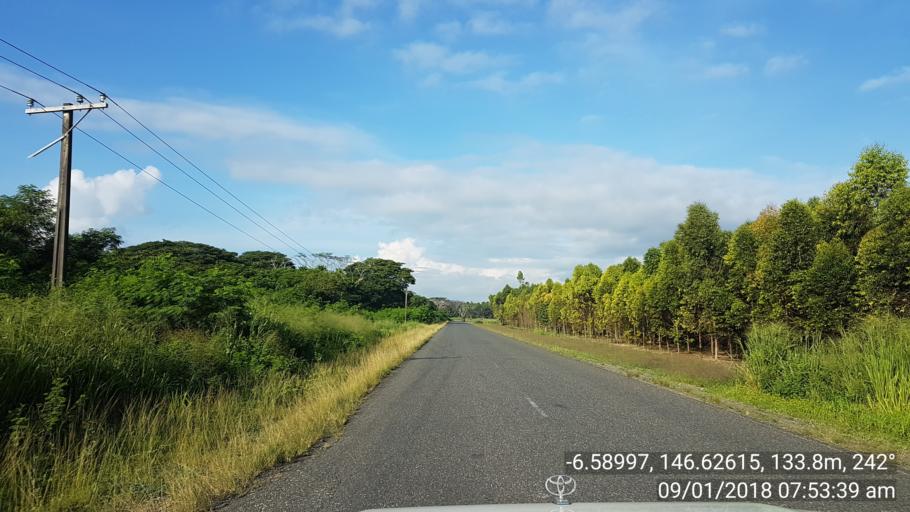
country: PG
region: Morobe
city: Lae
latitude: -6.5900
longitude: 146.6261
